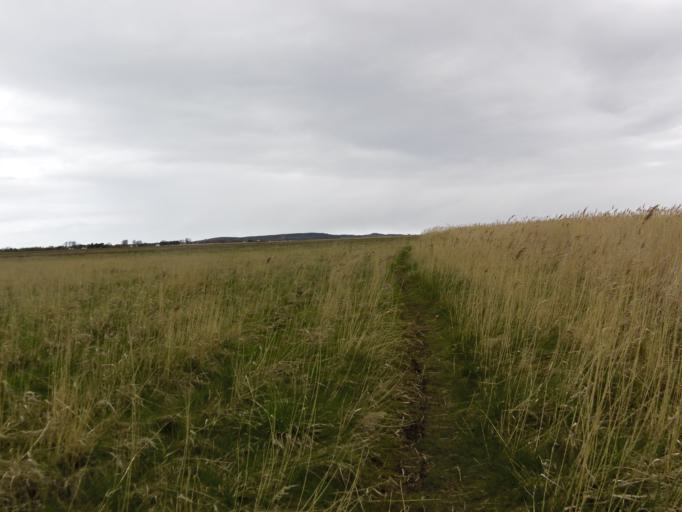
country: DE
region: Mecklenburg-Vorpommern
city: Hiddensee
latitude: 54.5477
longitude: 13.1142
